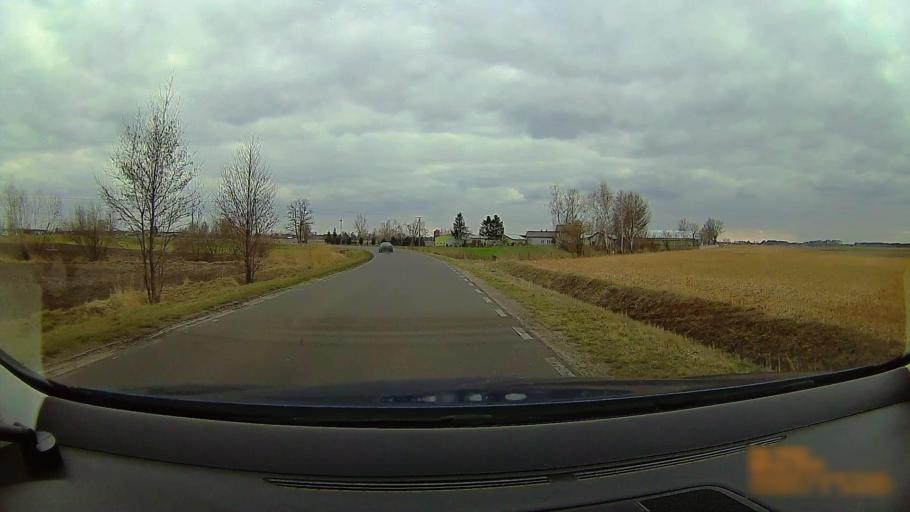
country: PL
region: Greater Poland Voivodeship
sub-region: Powiat koninski
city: Rzgow Pierwszy
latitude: 52.1144
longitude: 18.0727
